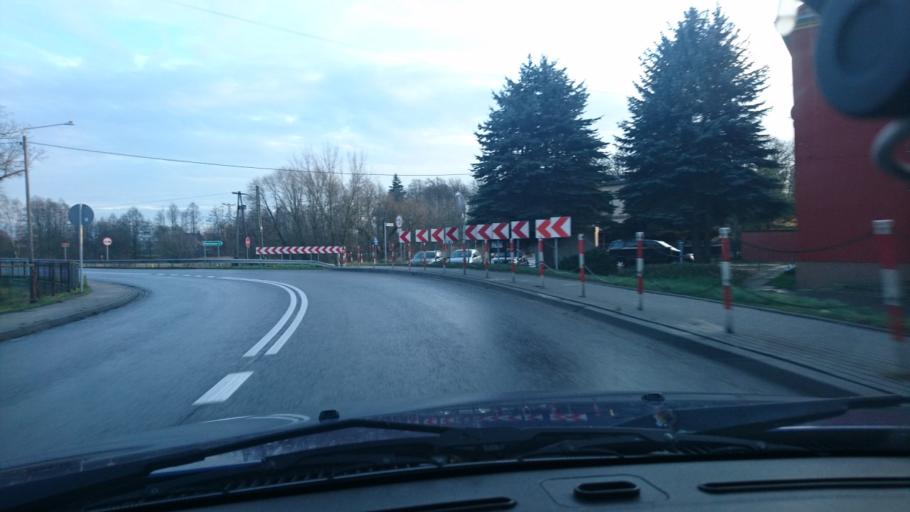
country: PL
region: Greater Poland Voivodeship
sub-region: Powiat kepinski
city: Opatow
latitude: 51.1656
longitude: 18.1477
